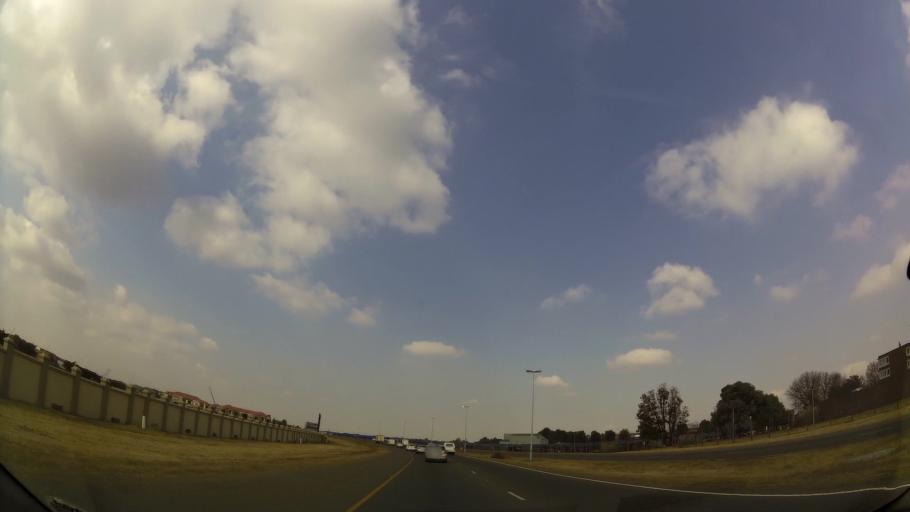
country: ZA
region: Gauteng
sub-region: Ekurhuleni Metropolitan Municipality
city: Benoni
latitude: -26.1443
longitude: 28.2692
